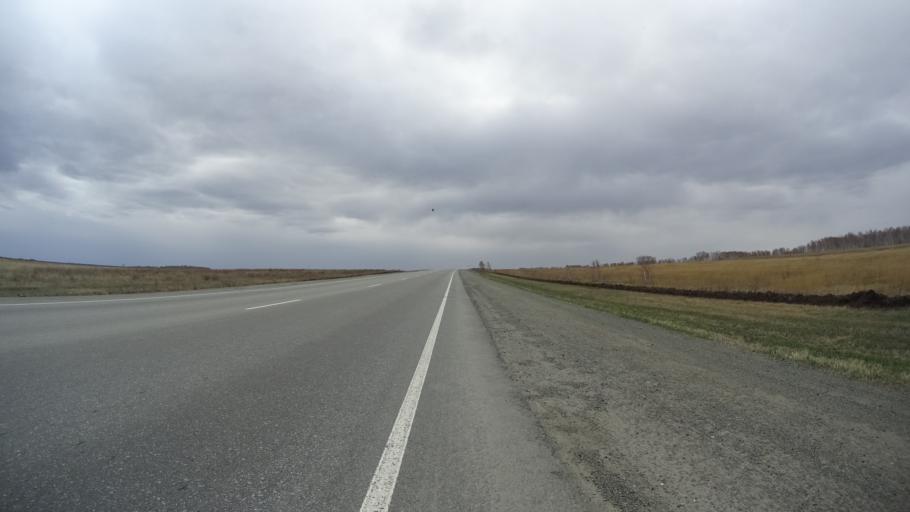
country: RU
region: Chelyabinsk
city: Yemanzhelinsk
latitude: 54.7086
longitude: 61.2585
